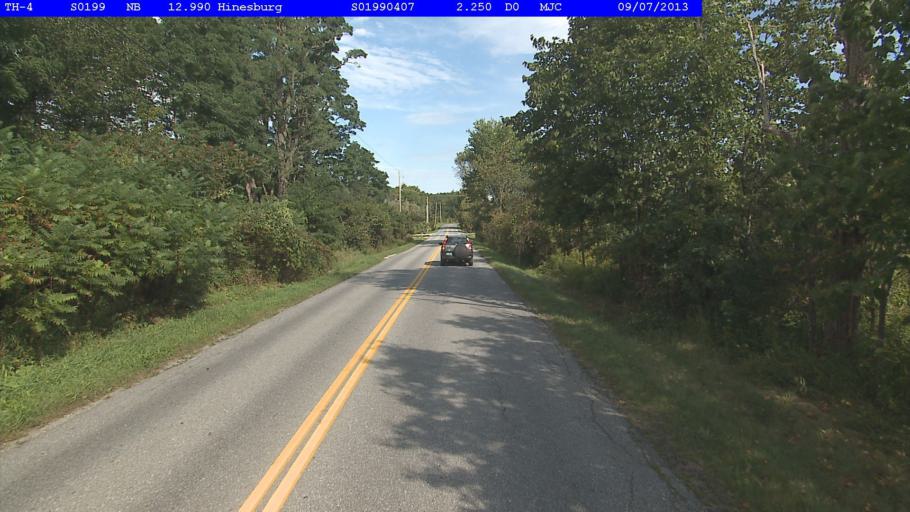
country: US
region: Vermont
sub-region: Chittenden County
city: Hinesburg
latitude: 44.3103
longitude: -73.1097
